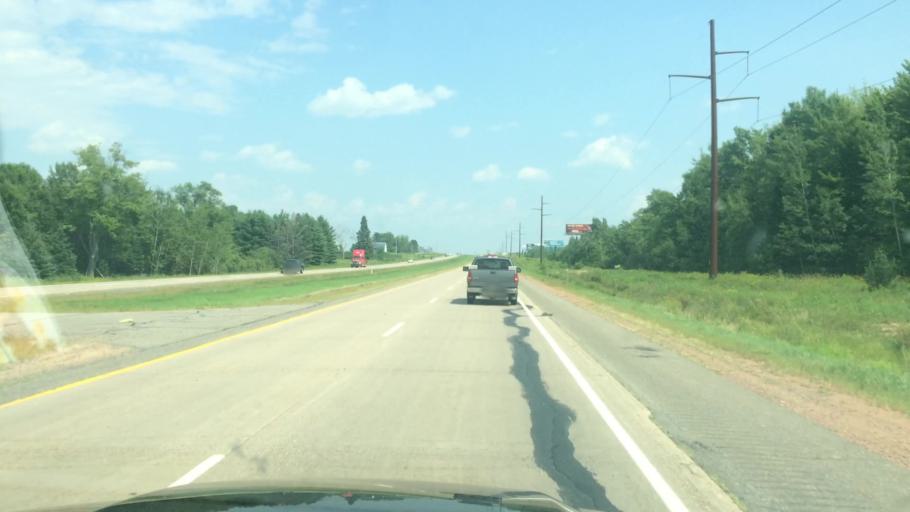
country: US
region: Wisconsin
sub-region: Marathon County
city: Edgar
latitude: 44.9441
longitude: -90.0163
